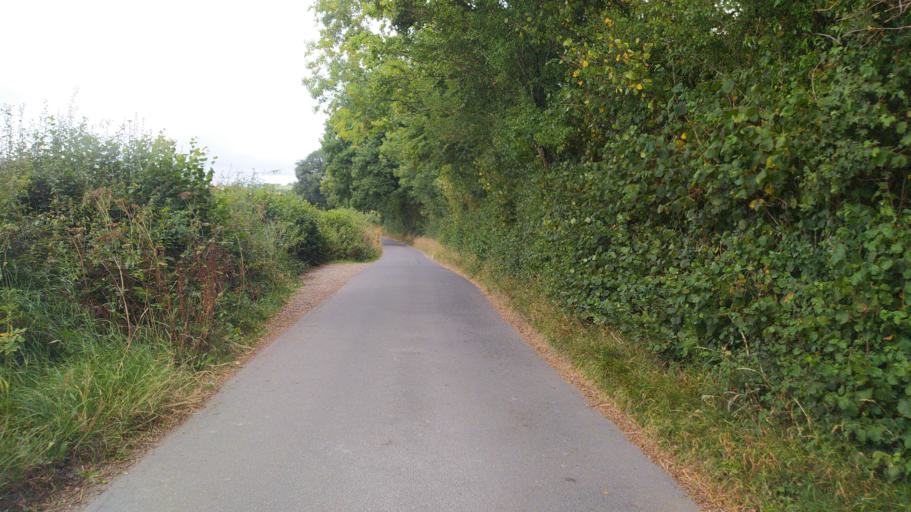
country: GB
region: England
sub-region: Hampshire
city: Petersfield
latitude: 50.9883
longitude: -0.9734
